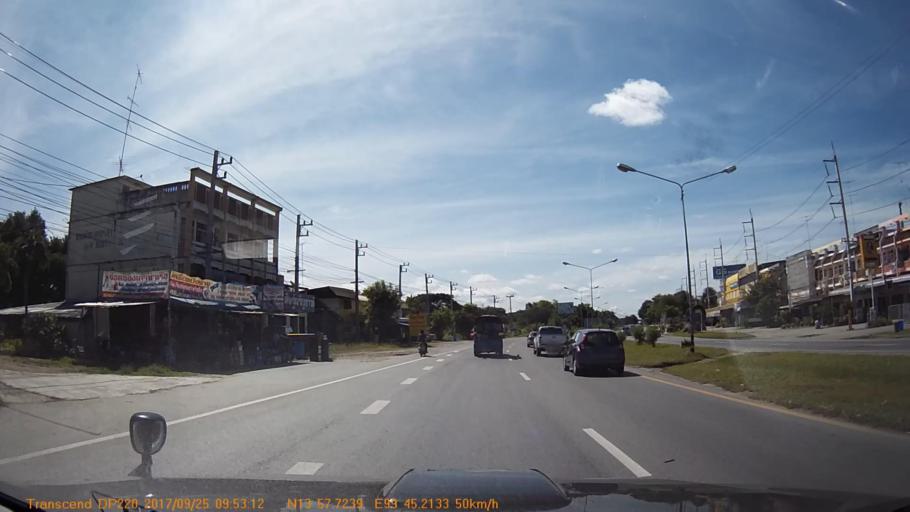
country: TH
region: Kanchanaburi
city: Tha Maka
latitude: 13.9619
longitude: 99.7537
